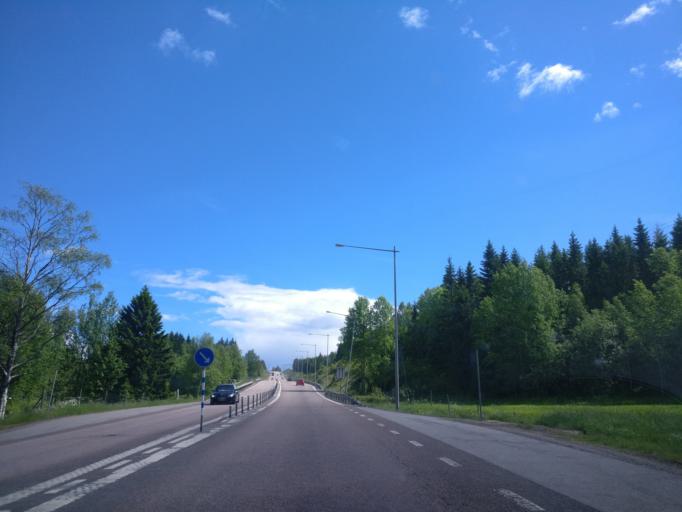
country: SE
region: Vaesternorrland
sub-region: Haernoesands Kommun
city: Haernoesand
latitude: 62.6586
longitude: 17.8636
